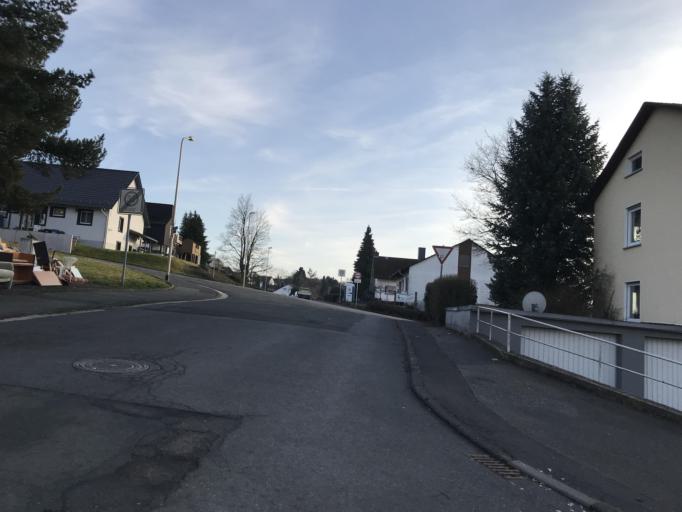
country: DE
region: Hesse
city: Weilburg
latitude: 50.4850
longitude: 8.2760
